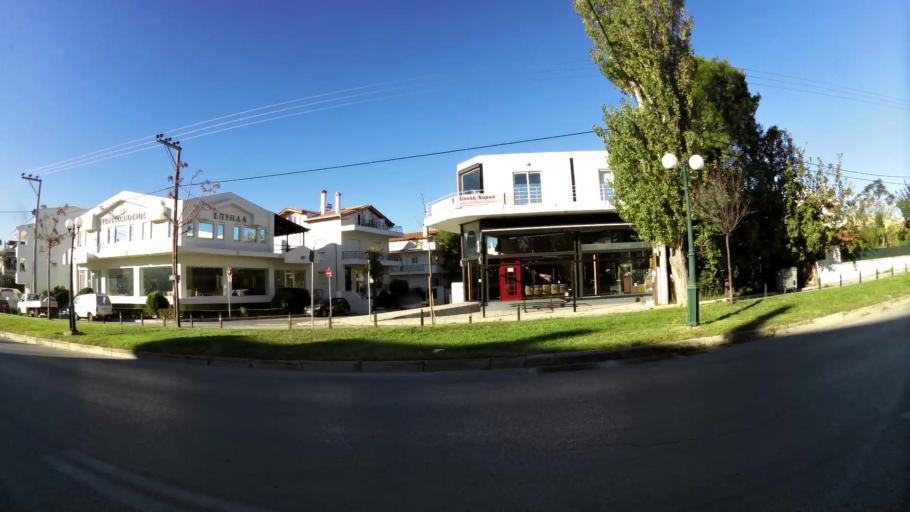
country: GR
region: Attica
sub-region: Nomarchia Anatolikis Attikis
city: Gerakas
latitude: 38.0137
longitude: 23.8538
